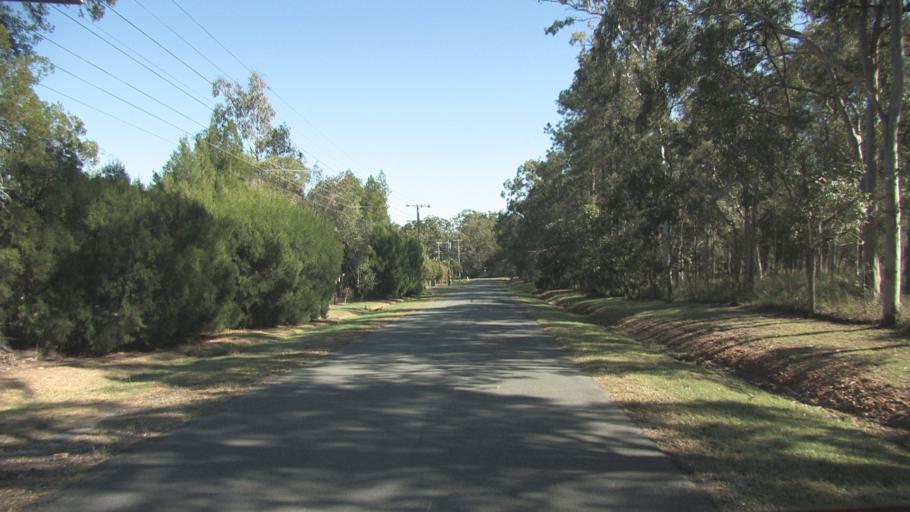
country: AU
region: Queensland
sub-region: Logan
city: Park Ridge South
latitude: -27.6938
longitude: 153.0066
